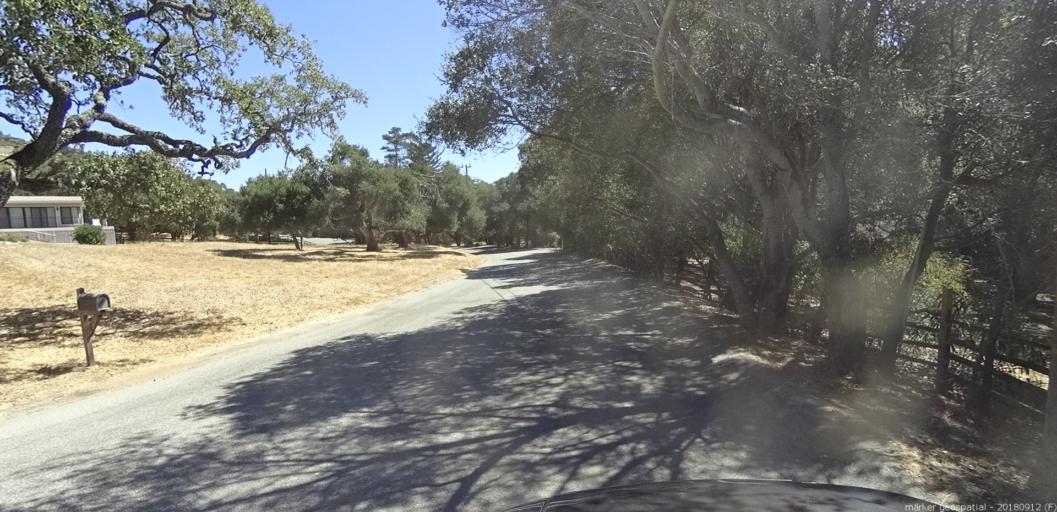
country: US
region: California
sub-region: Monterey County
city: Carmel Valley Village
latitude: 36.4986
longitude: -121.7494
